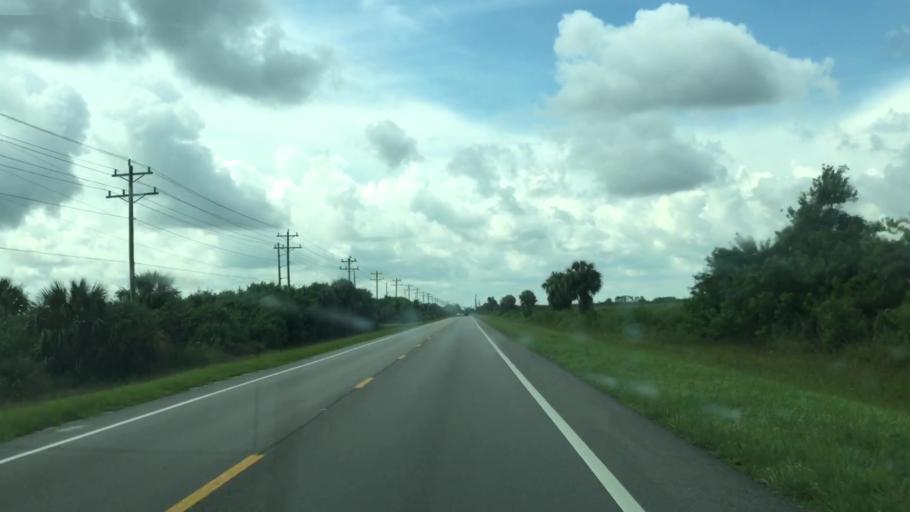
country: US
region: Florida
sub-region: Collier County
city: Immokalee
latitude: 26.3836
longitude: -81.4171
